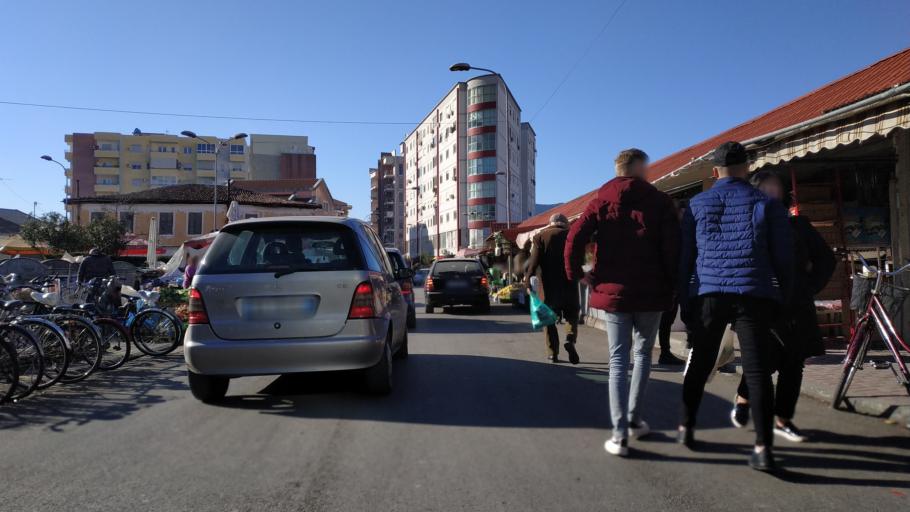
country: AL
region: Shkoder
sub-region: Rrethi i Shkodres
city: Shkoder
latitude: 42.0686
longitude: 19.5076
